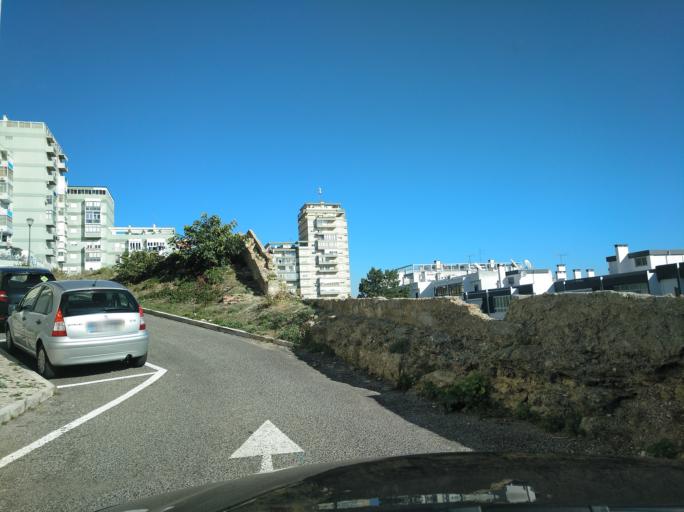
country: PT
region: Lisbon
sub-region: Lisbon
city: Lisbon
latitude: 38.7231
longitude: -9.1167
